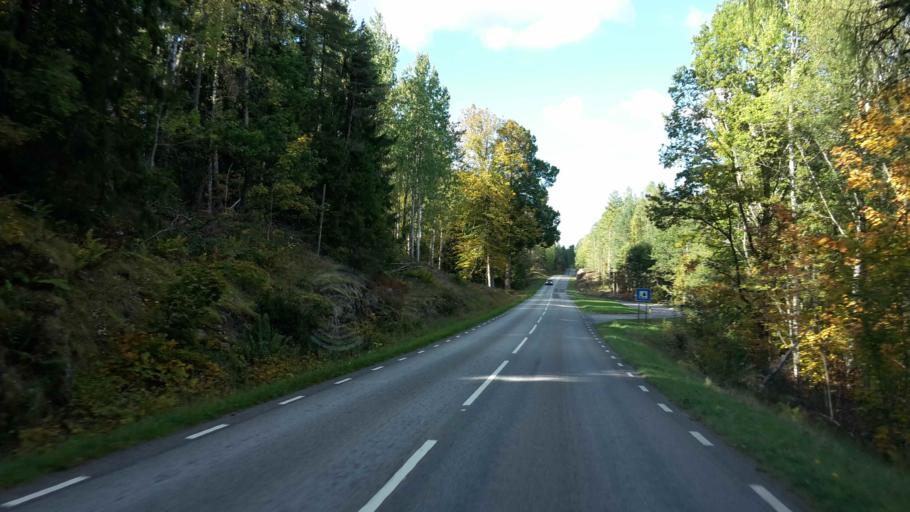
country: SE
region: OEstergoetland
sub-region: Atvidabergs Kommun
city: Atvidaberg
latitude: 58.1675
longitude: 16.1416
